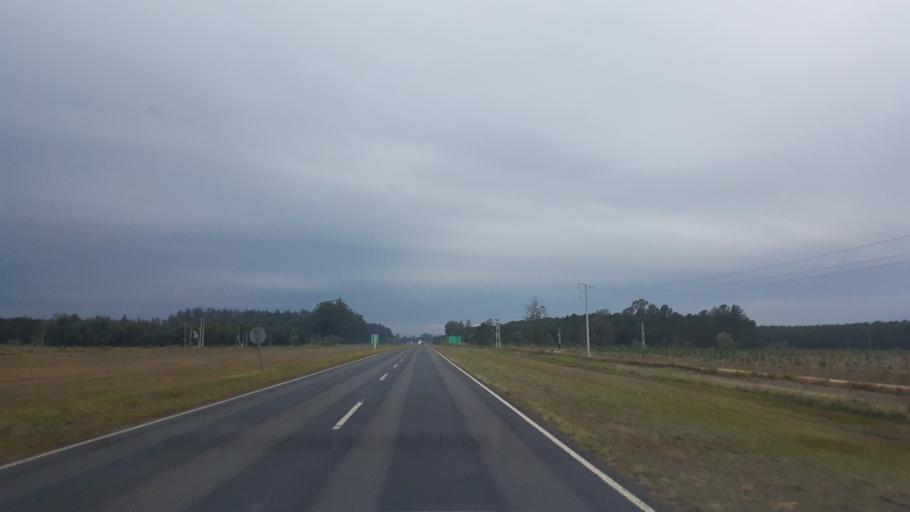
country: AR
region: Corrientes
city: Ituzaingo
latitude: -27.6063
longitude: -56.4444
